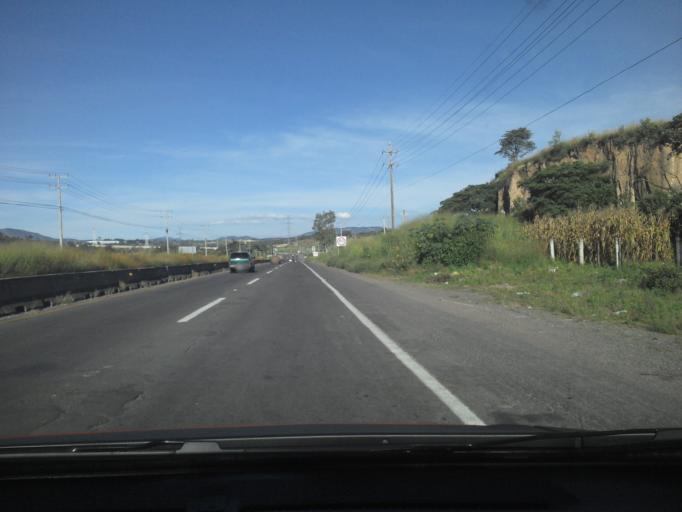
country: MX
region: Jalisco
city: Tala
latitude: 20.6774
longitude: -103.7025
